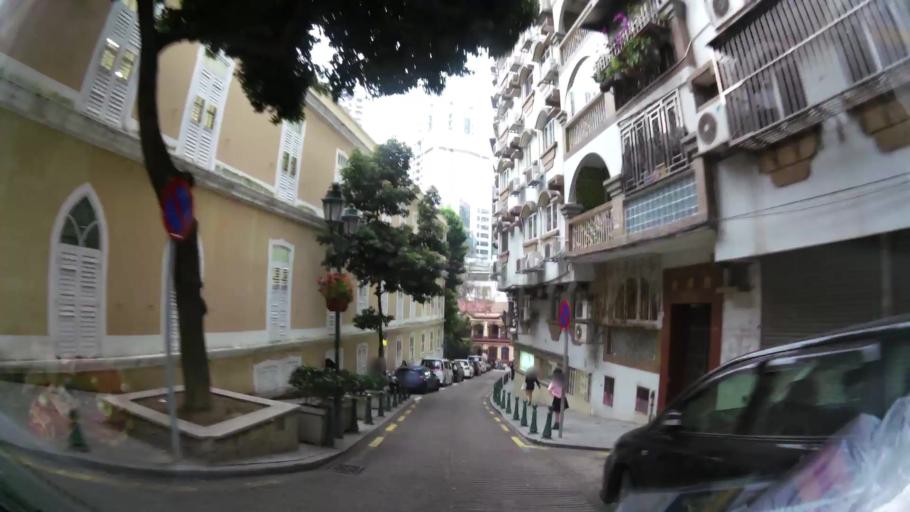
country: MO
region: Macau
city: Macau
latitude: 22.1954
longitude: 113.5431
